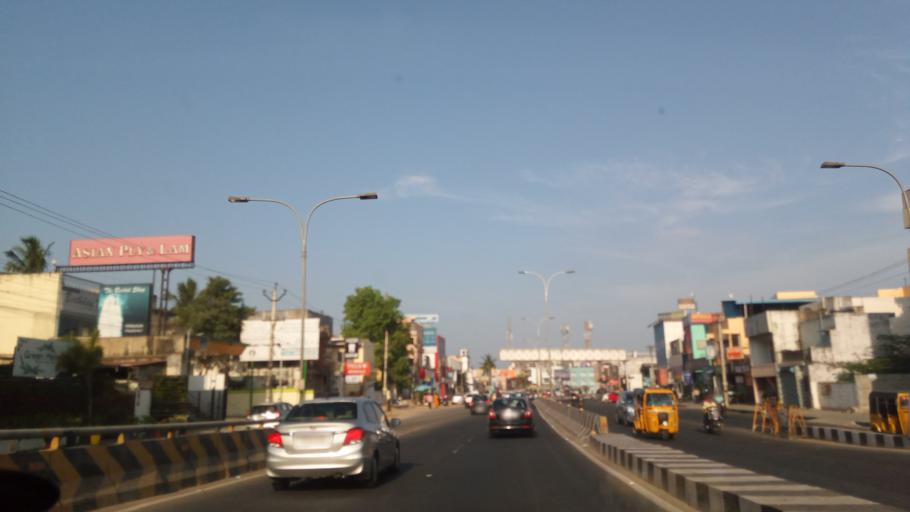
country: IN
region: Tamil Nadu
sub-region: Thiruvallur
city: Porur
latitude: 13.0344
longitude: 80.1580
